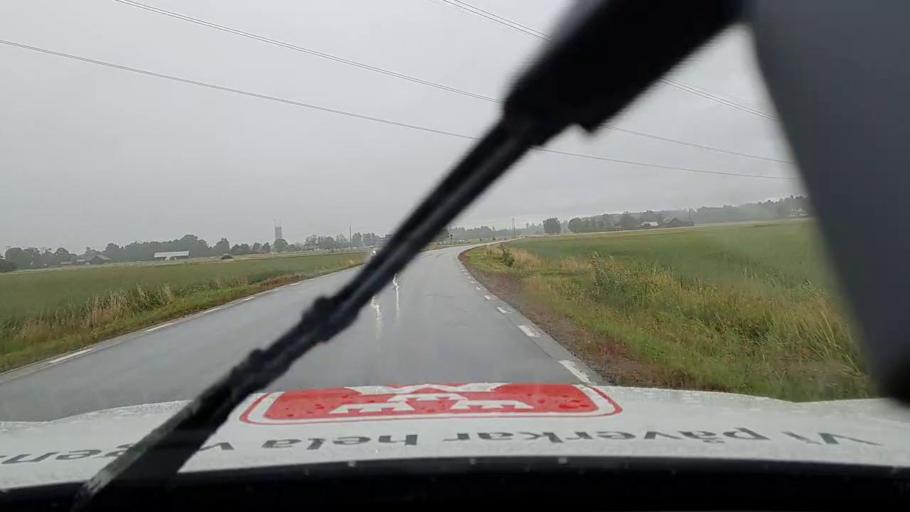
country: SE
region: Vaestra Goetaland
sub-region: Toreboda Kommun
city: Toereboda
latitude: 58.6901
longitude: 14.1277
